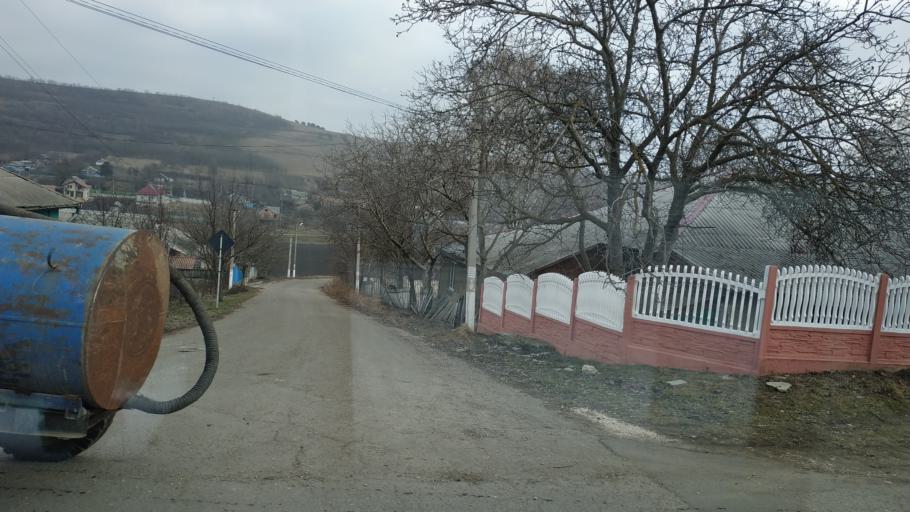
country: MD
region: Hincesti
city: Dancu
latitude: 46.8864
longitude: 28.3220
